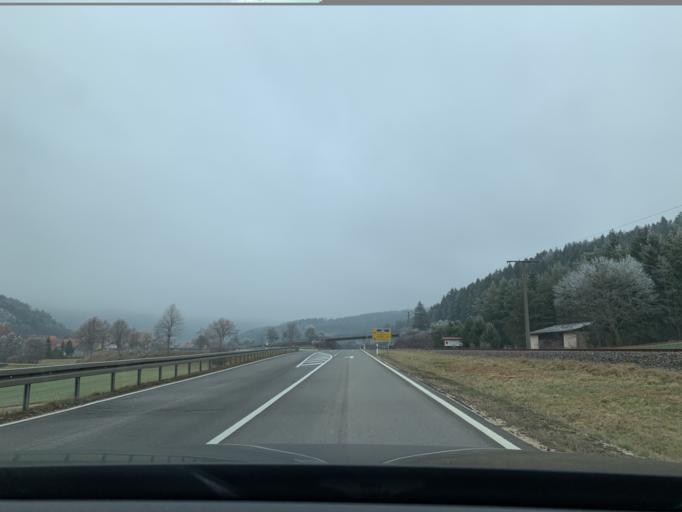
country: DE
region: Baden-Wuerttemberg
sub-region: Freiburg Region
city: Geisingen
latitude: 47.9029
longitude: 8.6722
